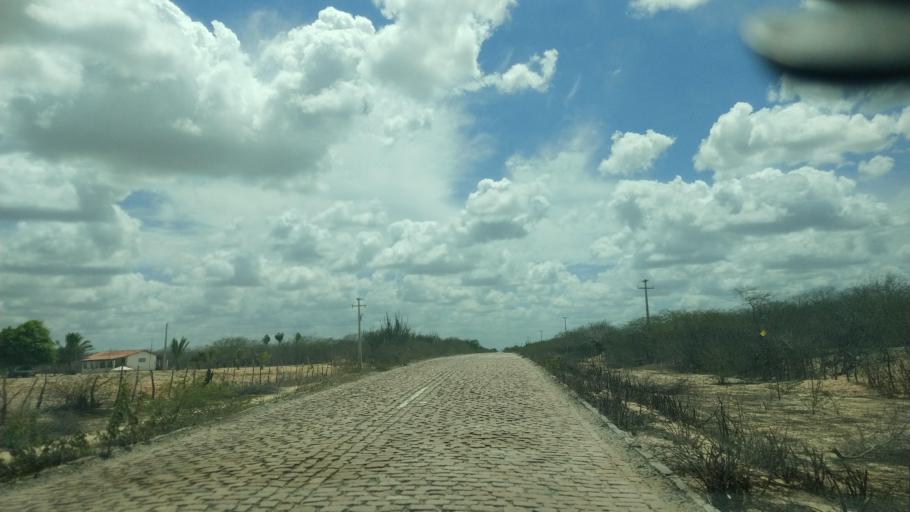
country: BR
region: Rio Grande do Norte
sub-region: Sao Paulo Do Potengi
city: Sao Paulo do Potengi
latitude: -5.9650
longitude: -35.8511
